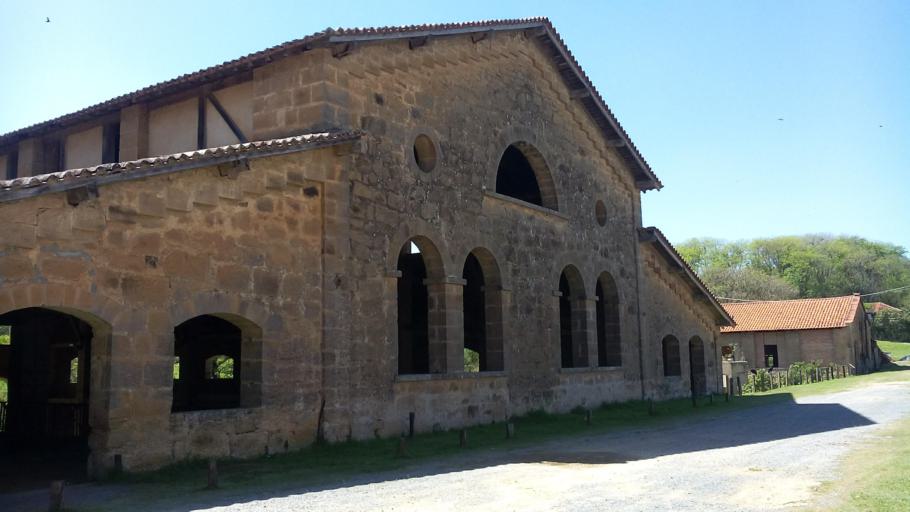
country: BR
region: Sao Paulo
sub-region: Aracoiaba Da Serra
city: Aracoiaba da Serra
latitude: -23.4260
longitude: -47.5964
